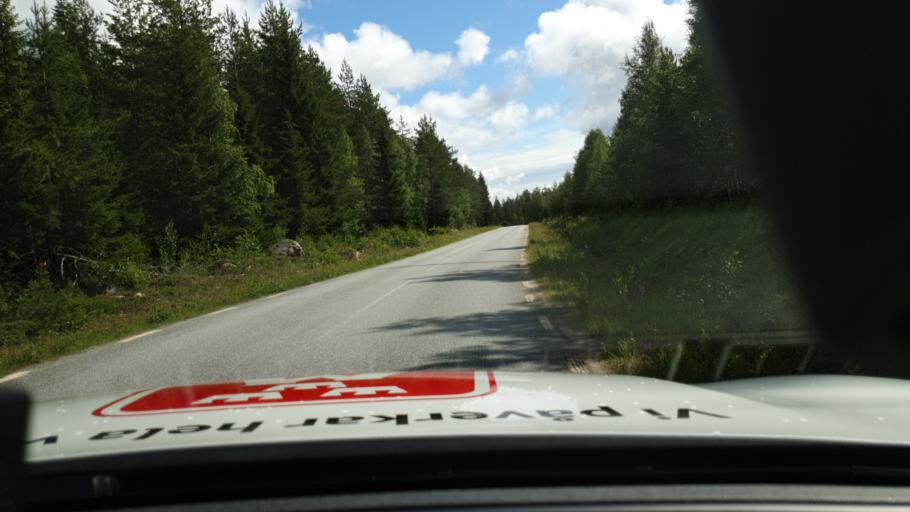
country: SE
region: Norrbotten
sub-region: Pitea Kommun
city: Rosvik
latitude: 65.4352
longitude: 21.8667
